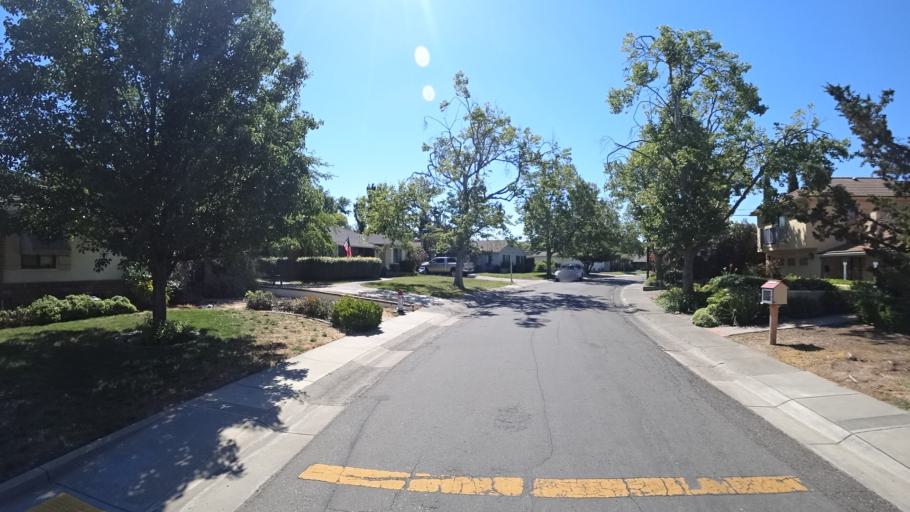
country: US
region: California
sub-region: Sacramento County
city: Parkway
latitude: 38.5290
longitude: -121.4923
